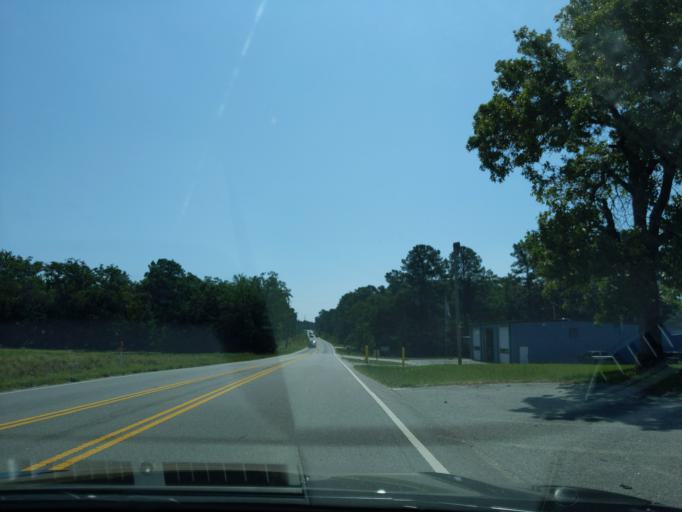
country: US
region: South Carolina
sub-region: Lexington County
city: Red Bank
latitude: 33.9317
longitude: -81.3061
